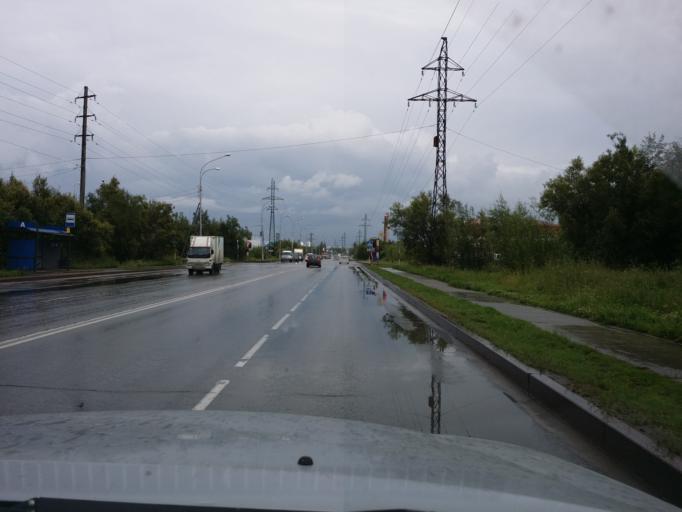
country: RU
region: Khanty-Mansiyskiy Avtonomnyy Okrug
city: Nizhnevartovsk
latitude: 60.9493
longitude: 76.5114
